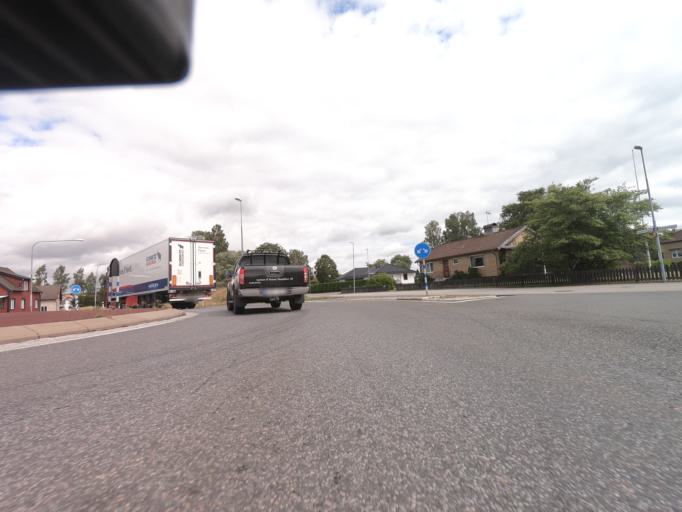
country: SE
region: Joenkoeping
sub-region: Vaggeryds Kommun
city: Vaggeryd
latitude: 57.5129
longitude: 14.2794
